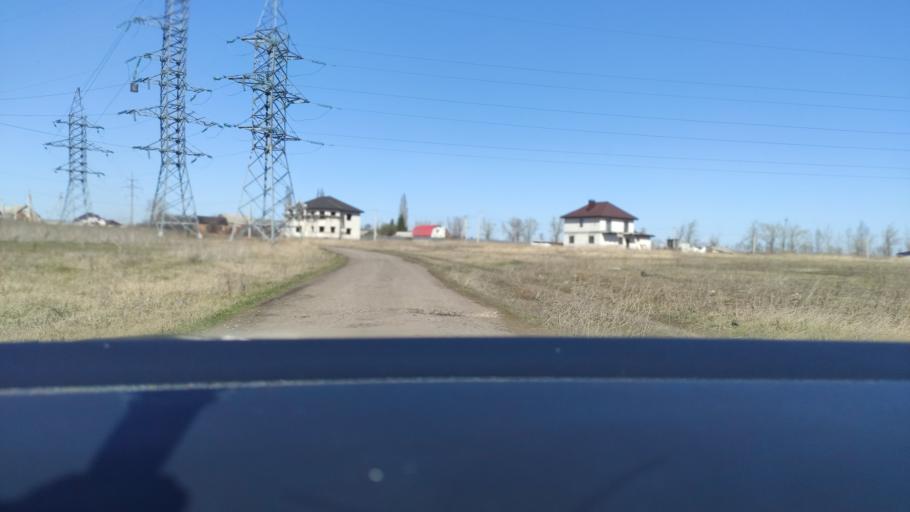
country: RU
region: Voronezj
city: Maslovka
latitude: 51.5018
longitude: 39.3055
